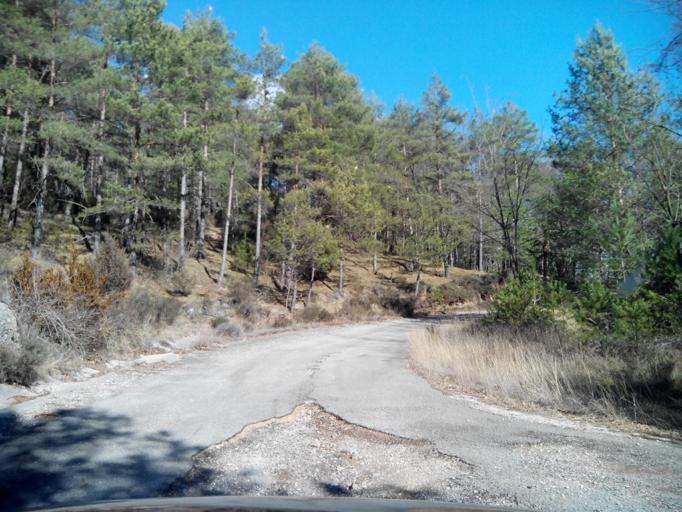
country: ES
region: Catalonia
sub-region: Provincia de Barcelona
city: Vilada
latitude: 42.1294
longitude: 1.9288
